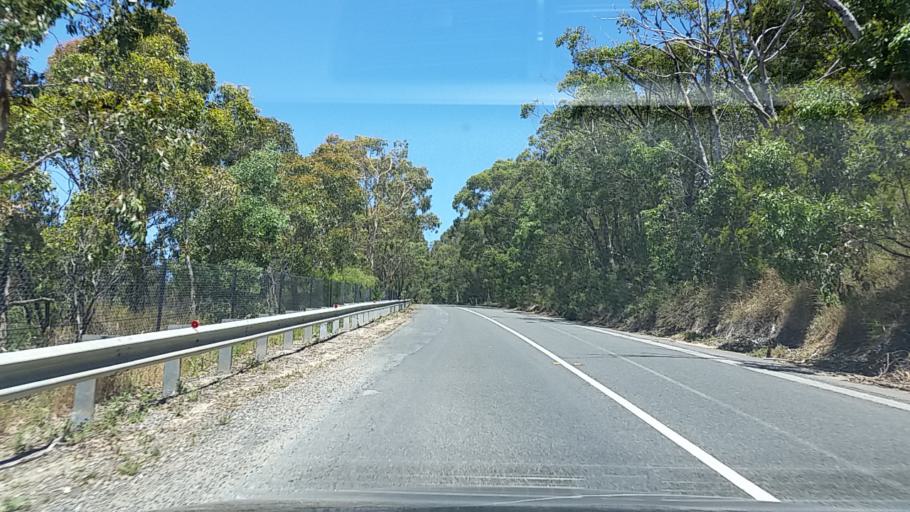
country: AU
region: South Australia
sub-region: Adelaide Hills
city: Crafers
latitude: -34.9906
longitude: 138.6944
